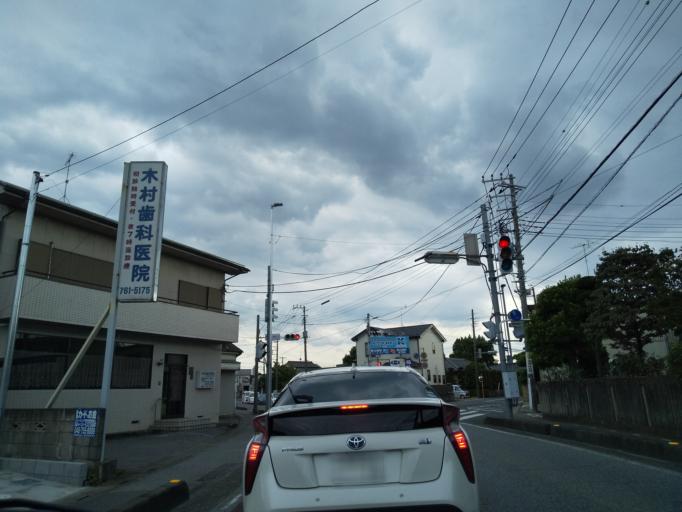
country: JP
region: Saitama
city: Kasukabe
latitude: 35.9867
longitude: 139.7687
